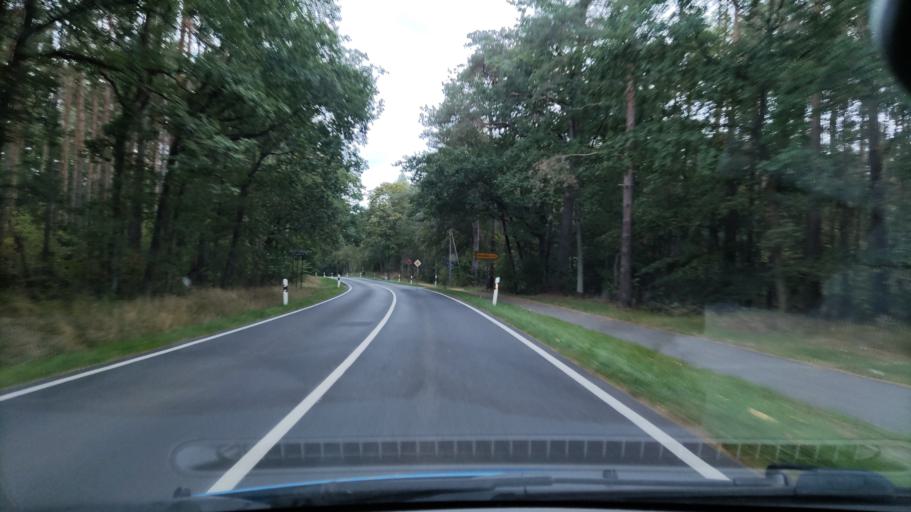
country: DE
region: Mecklenburg-Vorpommern
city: Lubtheen
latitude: 53.3797
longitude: 10.9676
